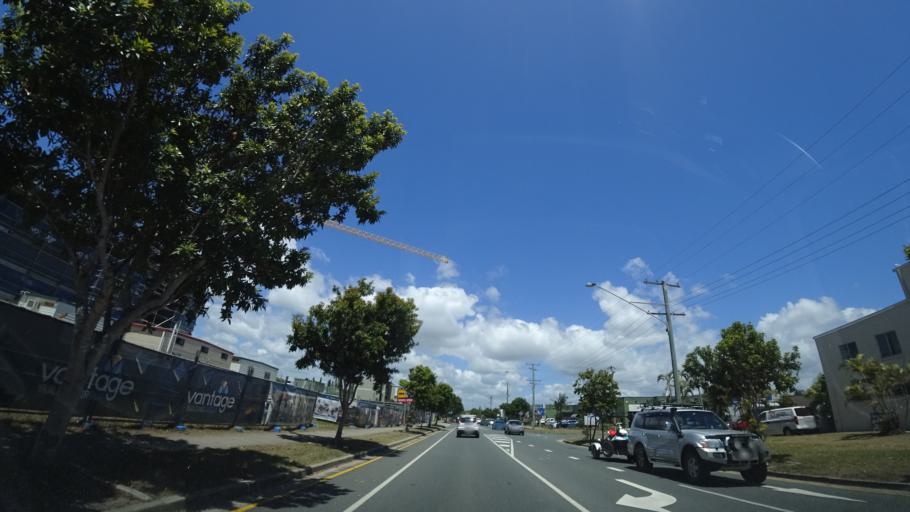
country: AU
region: Queensland
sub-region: Sunshine Coast
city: Mooloolaba
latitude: -26.7308
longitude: 153.1248
